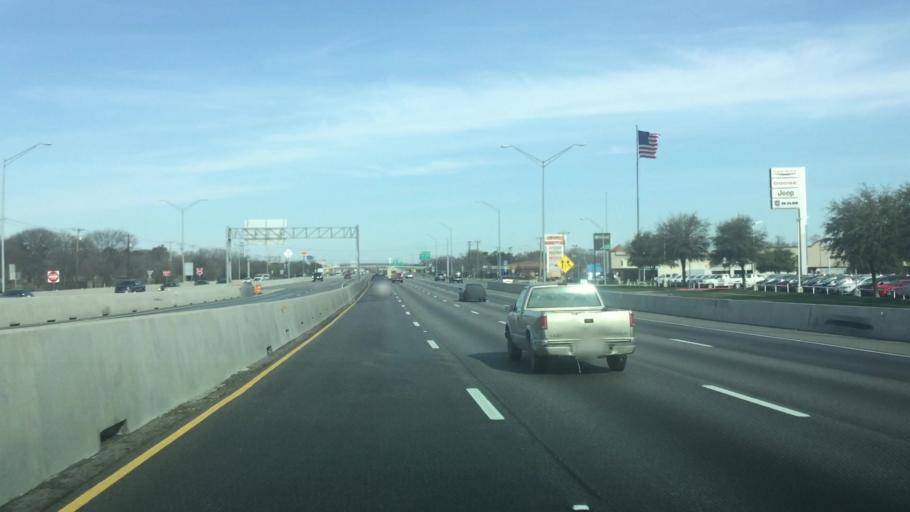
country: US
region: Texas
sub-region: Denton County
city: Lewisville
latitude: 33.0319
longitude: -96.9948
